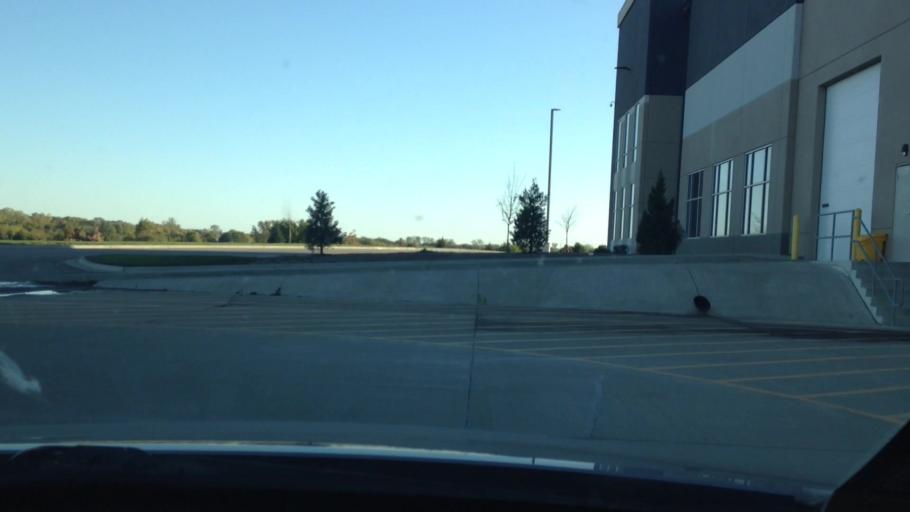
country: US
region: Kansas
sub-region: Johnson County
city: Gardner
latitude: 38.7728
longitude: -94.9431
